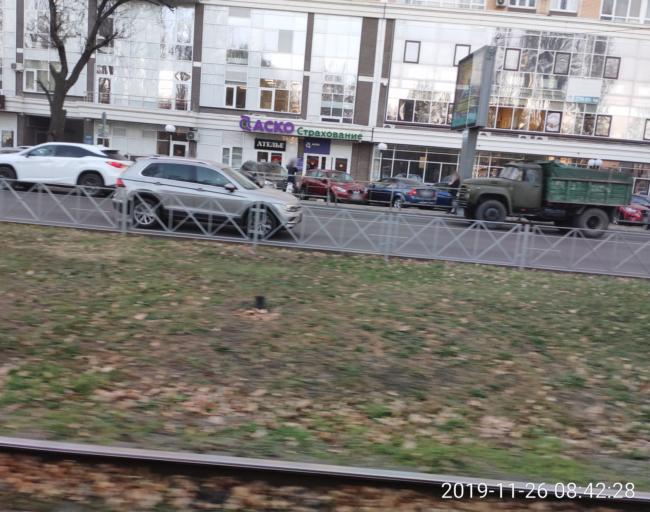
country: RU
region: Krasnodarskiy
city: Krasnodar
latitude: 45.0506
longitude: 38.9841
